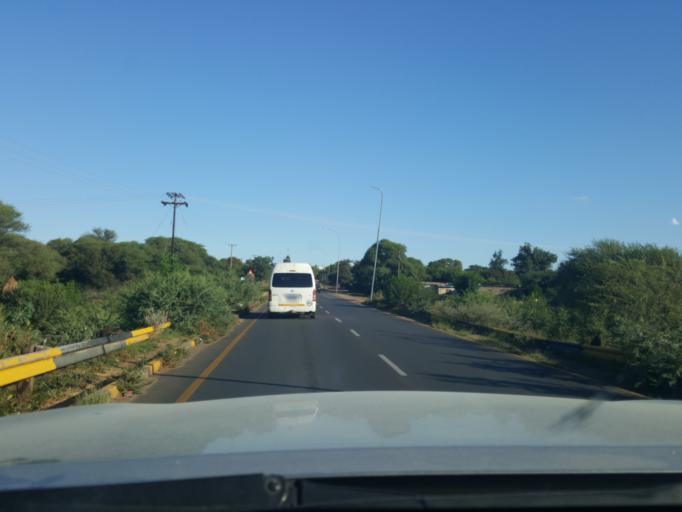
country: BW
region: South East
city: Gaborone
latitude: -24.6377
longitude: 25.9392
